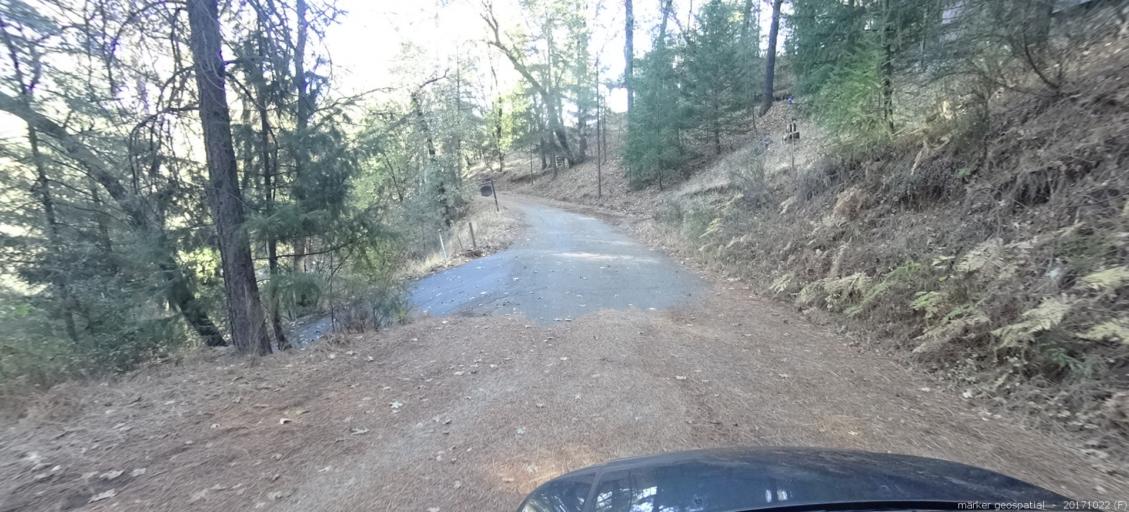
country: US
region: California
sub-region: Shasta County
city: Shasta Lake
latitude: 40.8402
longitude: -122.3684
